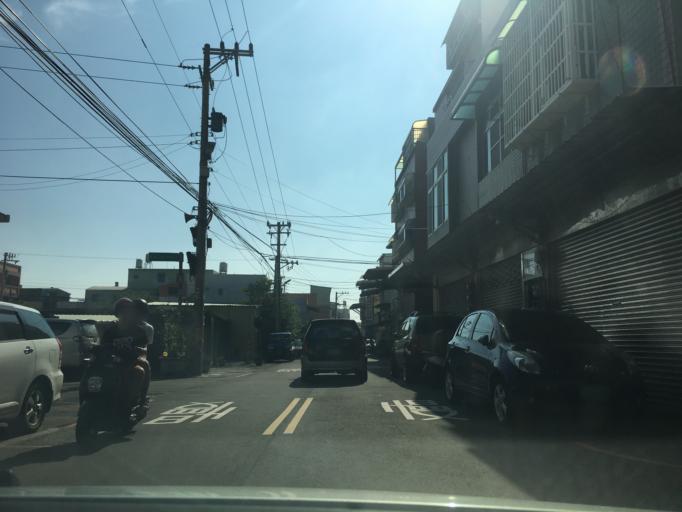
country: TW
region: Taiwan
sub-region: Hsinchu
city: Hsinchu
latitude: 24.8090
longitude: 120.9210
